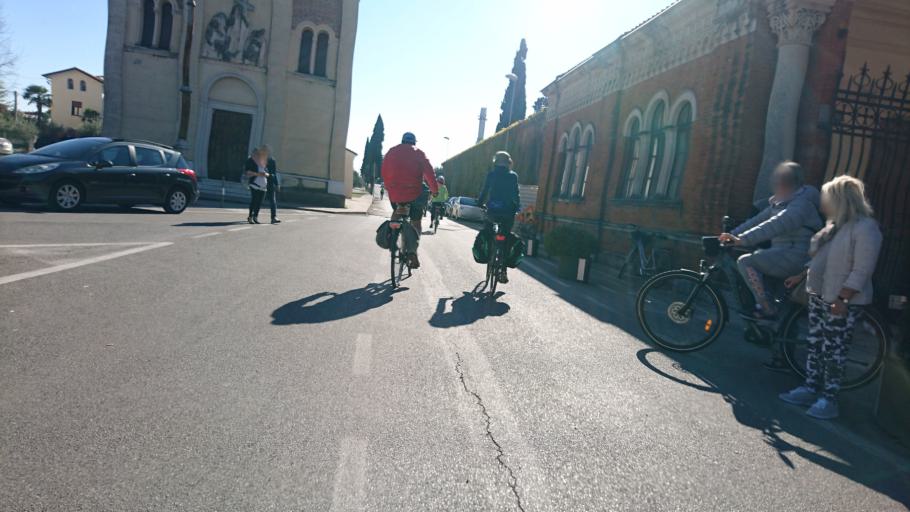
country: IT
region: Veneto
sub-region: Provincia di Vicenza
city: Bassano del Grappa
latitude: 45.7505
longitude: 11.7362
